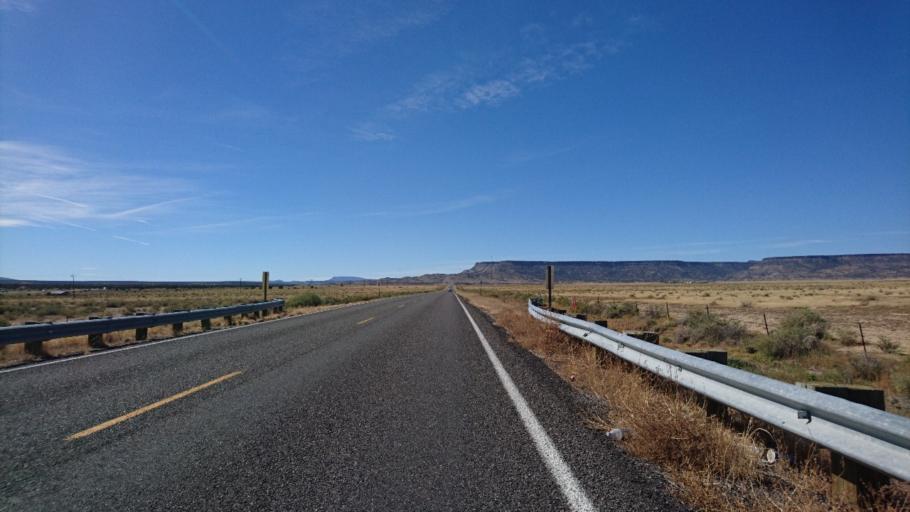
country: US
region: New Mexico
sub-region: Cibola County
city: Skyline-Ganipa
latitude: 35.0825
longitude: -107.6111
